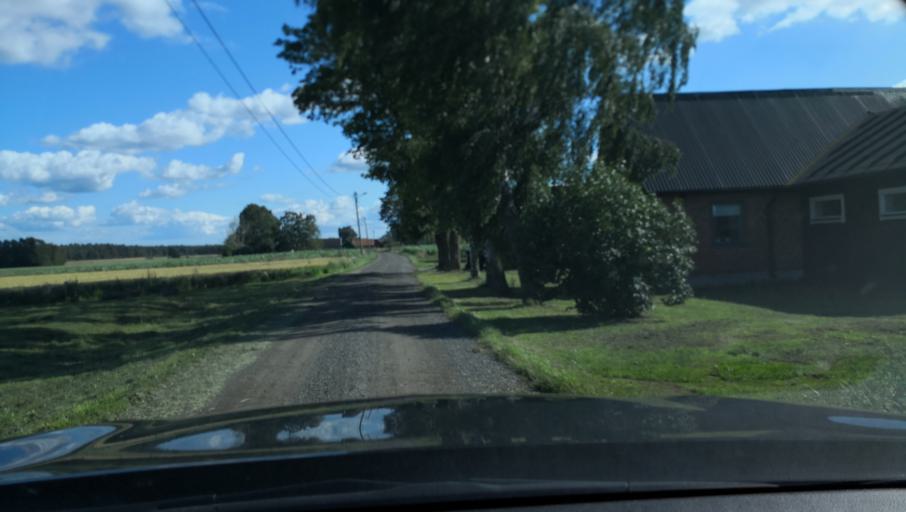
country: SE
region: Skane
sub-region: Kristianstads Kommun
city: Degeberga
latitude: 55.8120
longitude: 14.1890
